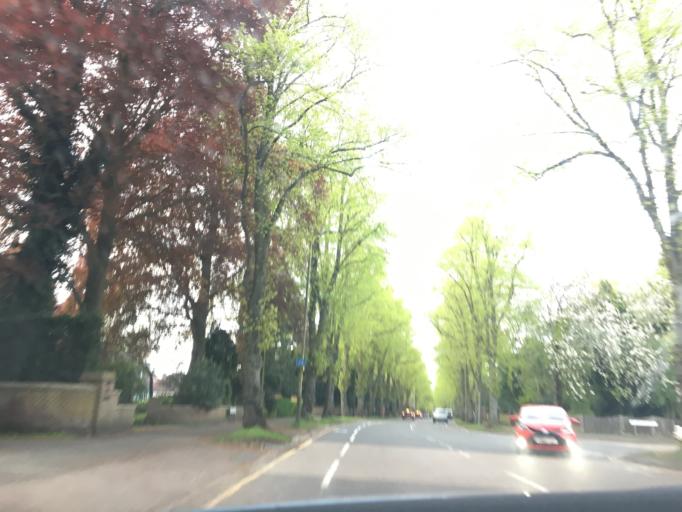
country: GB
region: England
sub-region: Leicestershire
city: Oadby
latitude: 52.6292
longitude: -1.0652
